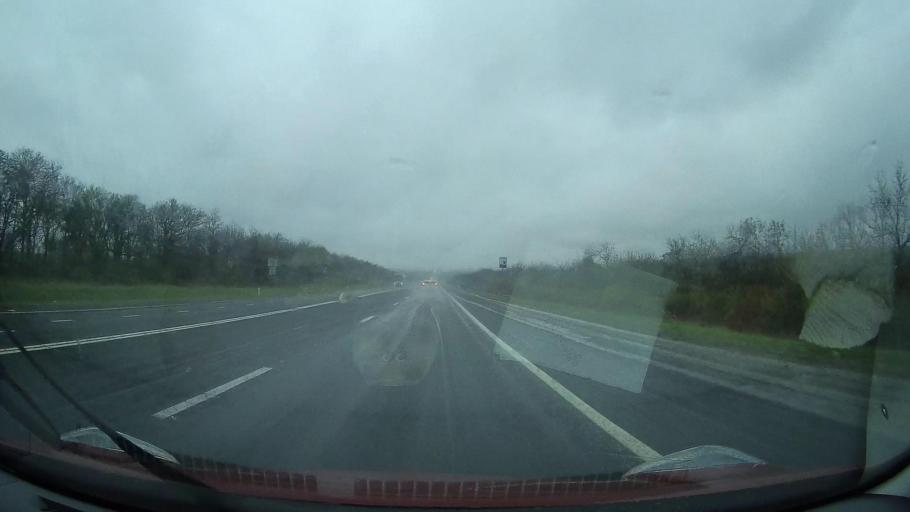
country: RU
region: Stavropol'skiy
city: Nevinnomyssk
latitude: 44.6211
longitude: 42.0850
